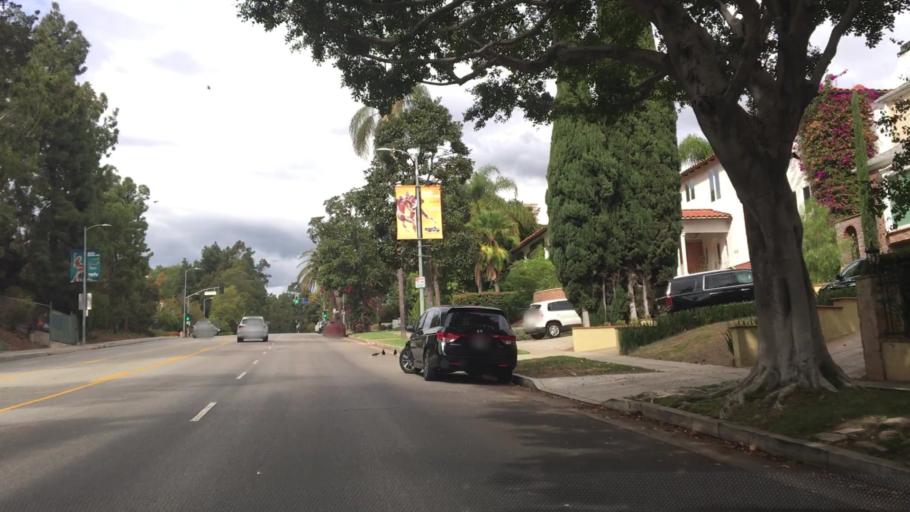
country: US
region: California
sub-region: Los Angeles County
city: Westwood, Los Angeles
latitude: 34.0730
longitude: -118.4373
